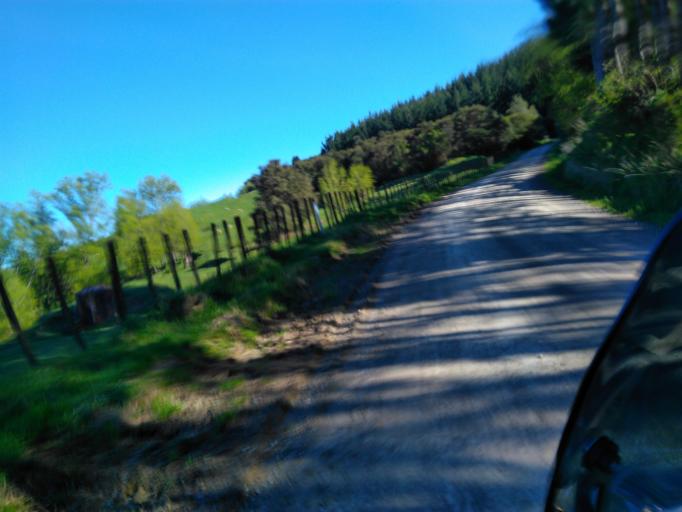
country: NZ
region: Gisborne
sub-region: Gisborne District
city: Gisborne
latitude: -38.4005
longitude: 177.6805
